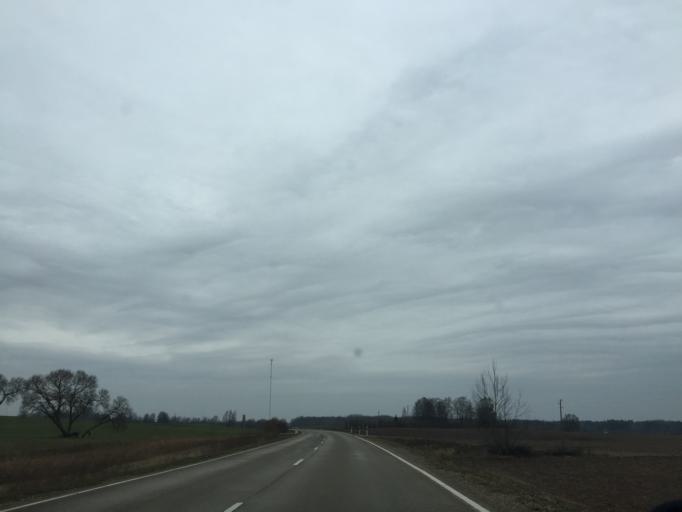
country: LV
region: Kandava
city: Kandava
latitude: 56.9205
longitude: 22.8221
